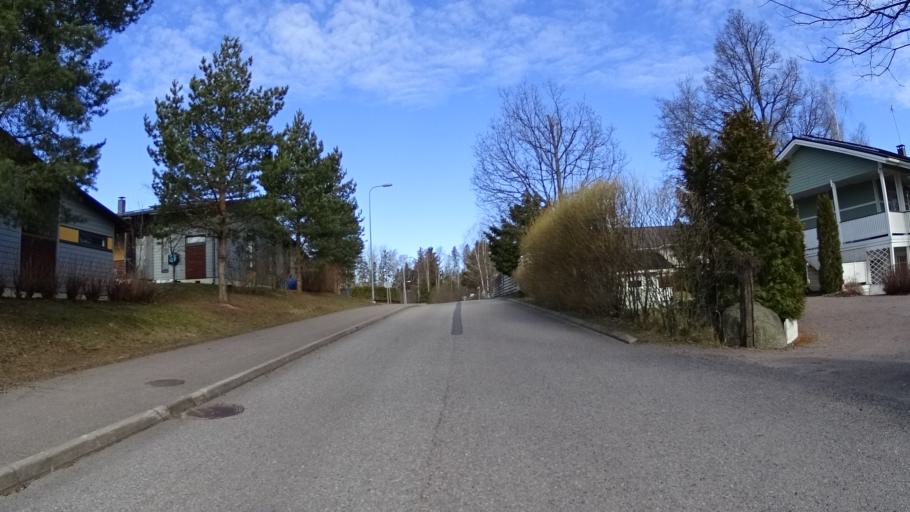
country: FI
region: Uusimaa
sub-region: Helsinki
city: Kauniainen
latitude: 60.2437
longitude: 24.7210
